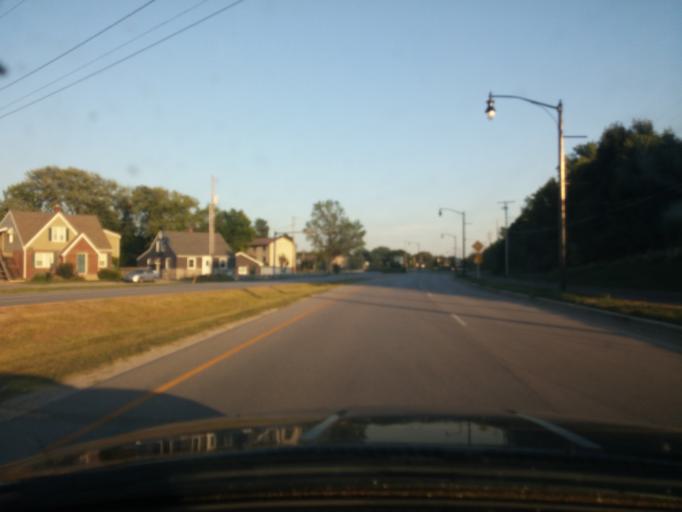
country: US
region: Indiana
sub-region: Tippecanoe County
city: West Lafayette
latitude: 40.4518
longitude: -86.9265
